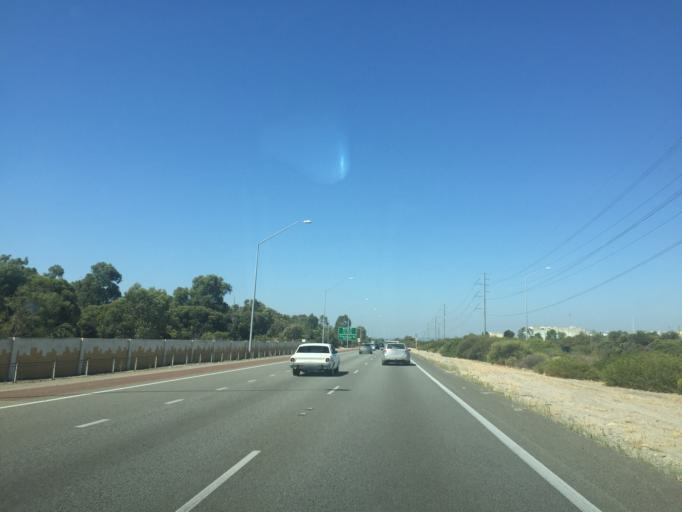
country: AU
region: Western Australia
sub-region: Canning
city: Willetton
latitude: -32.0641
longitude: 115.8958
